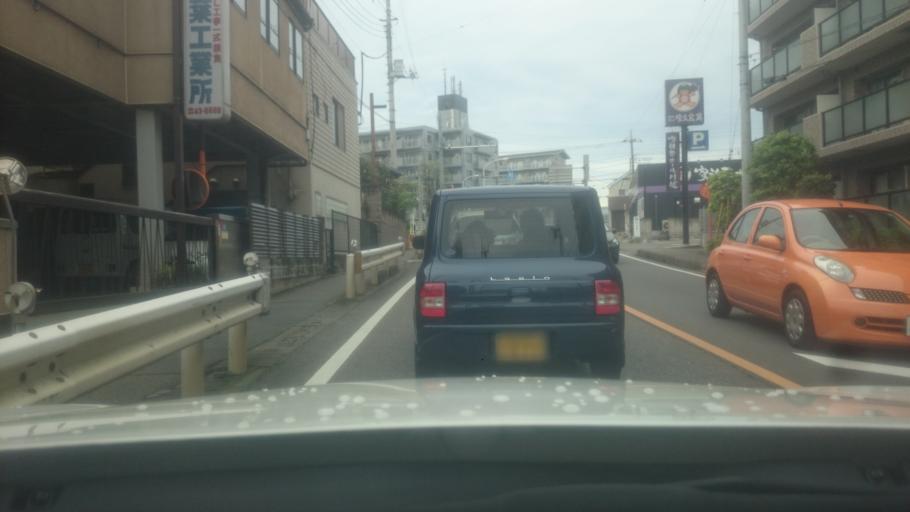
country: JP
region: Saitama
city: Kawagoe
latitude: 35.8998
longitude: 139.4883
